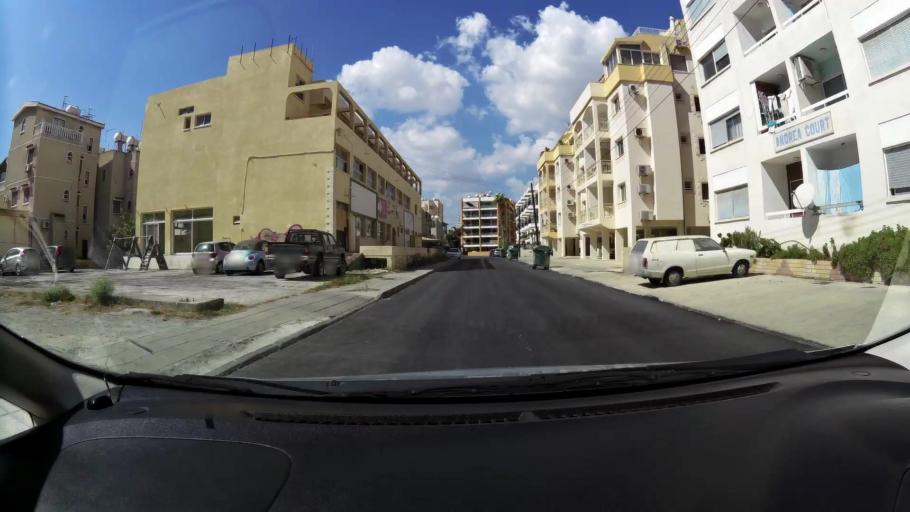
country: CY
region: Larnaka
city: Larnaca
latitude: 34.9014
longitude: 33.6359
